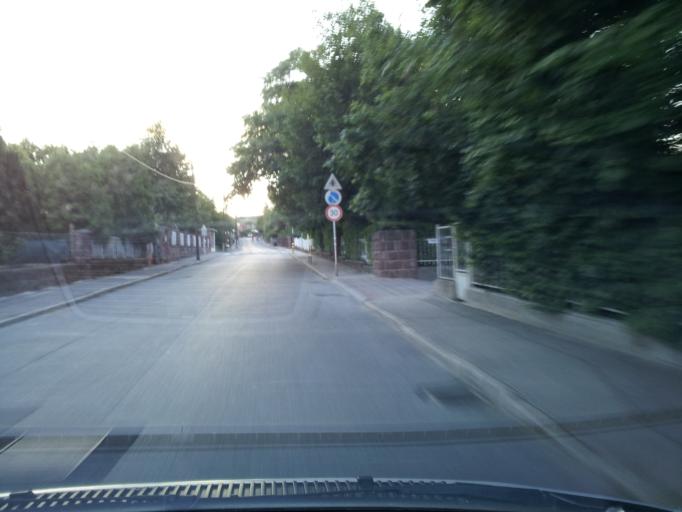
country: HU
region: Veszprem
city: Balatonalmadi
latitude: 47.0314
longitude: 18.0187
